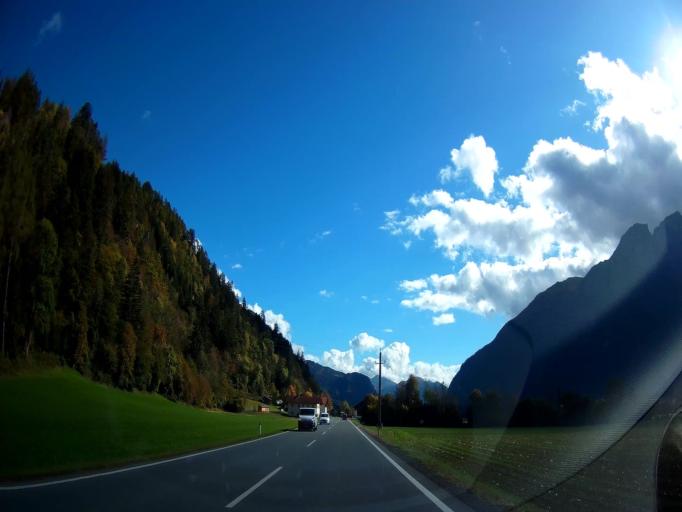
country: AT
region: Tyrol
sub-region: Politischer Bezirk Lienz
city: Lavant
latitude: 46.8097
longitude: 12.8523
